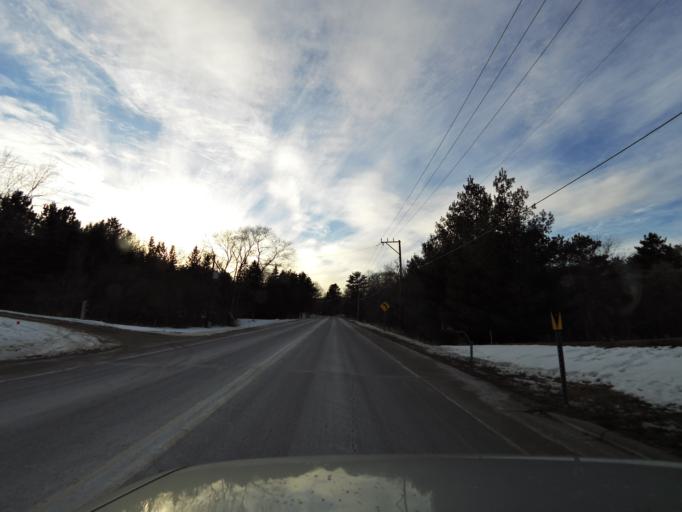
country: US
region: Minnesota
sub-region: Washington County
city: Afton
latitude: 44.9029
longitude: -92.7894
